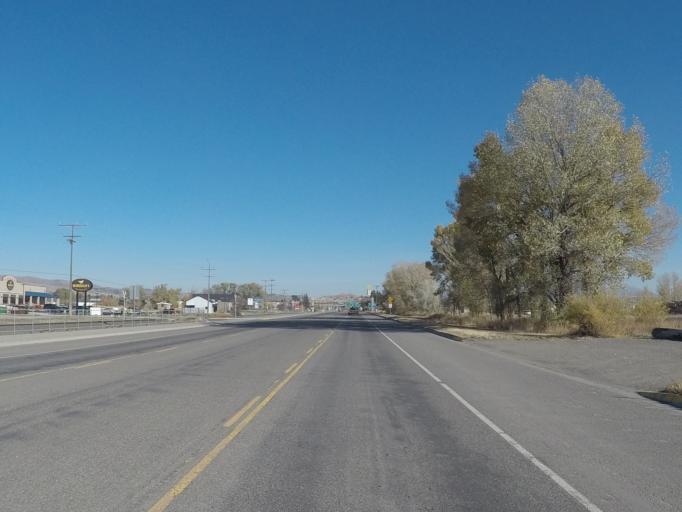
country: US
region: Montana
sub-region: Park County
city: Livingston
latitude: 45.6375
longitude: -110.5750
